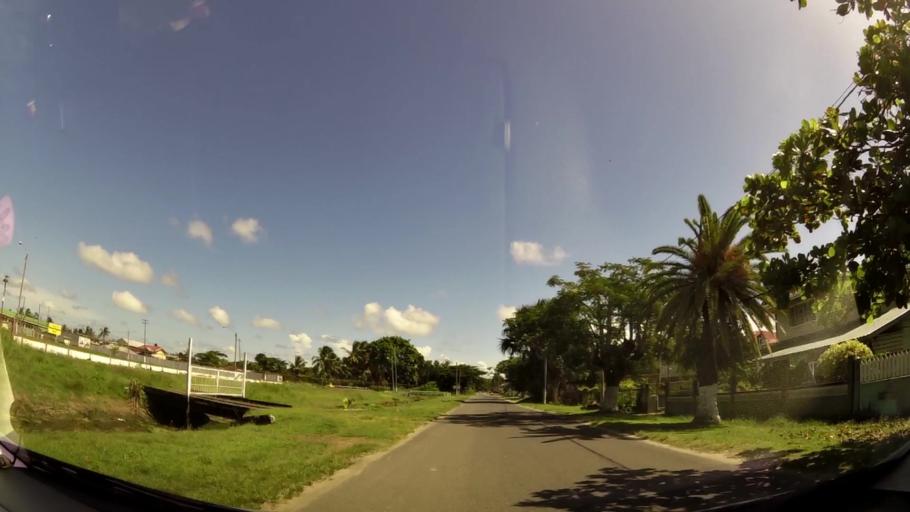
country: GY
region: Demerara-Mahaica
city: Georgetown
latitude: 6.8088
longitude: -58.1308
